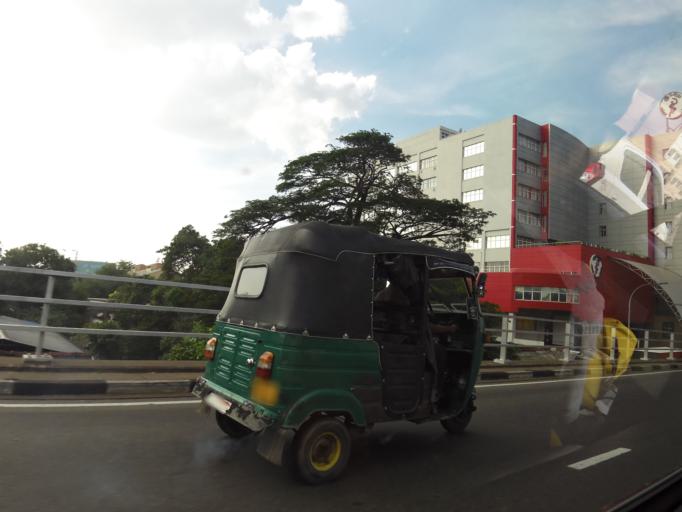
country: LK
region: Western
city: Kolonnawa
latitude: 6.9372
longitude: 79.8782
